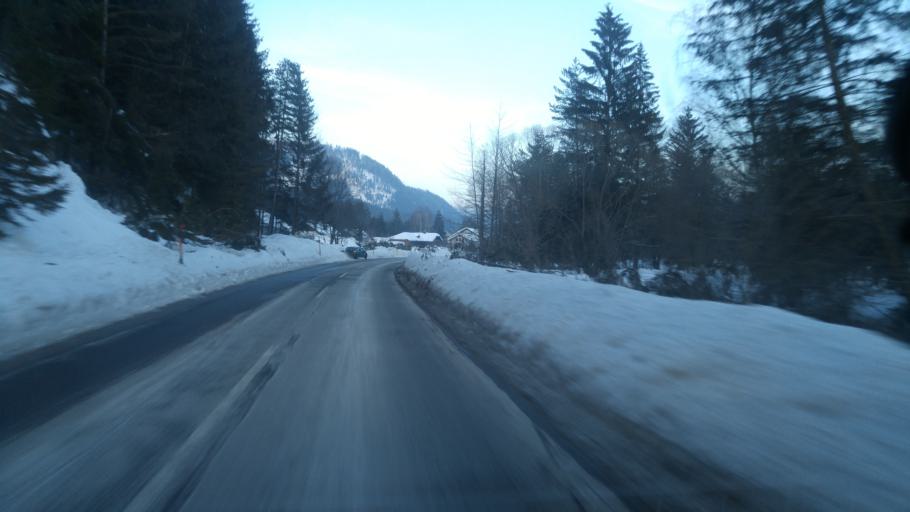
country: AT
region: Lower Austria
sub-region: Politischer Bezirk Wiener Neustadt
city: Rohr im Gebirge
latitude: 47.8856
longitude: 15.7136
